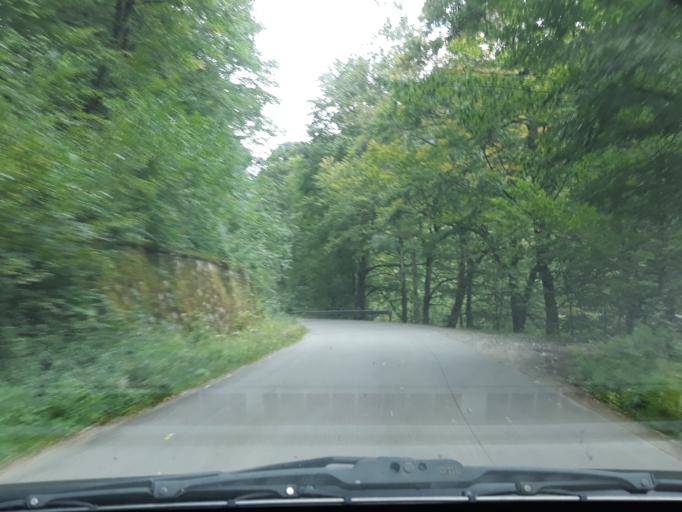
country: RO
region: Bihor
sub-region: Comuna Pietroasa
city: Pietroasa
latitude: 46.5875
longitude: 22.6196
